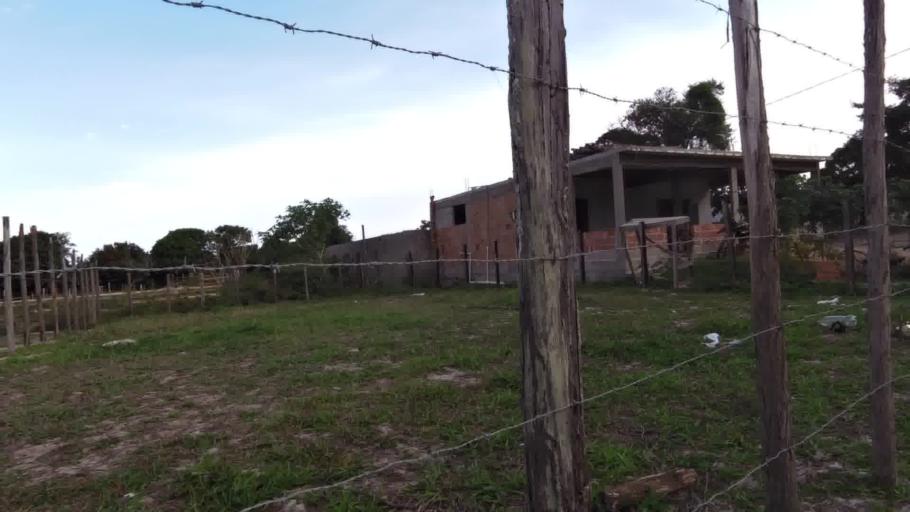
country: BR
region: Espirito Santo
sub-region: Piuma
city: Piuma
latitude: -20.8430
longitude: -40.7541
